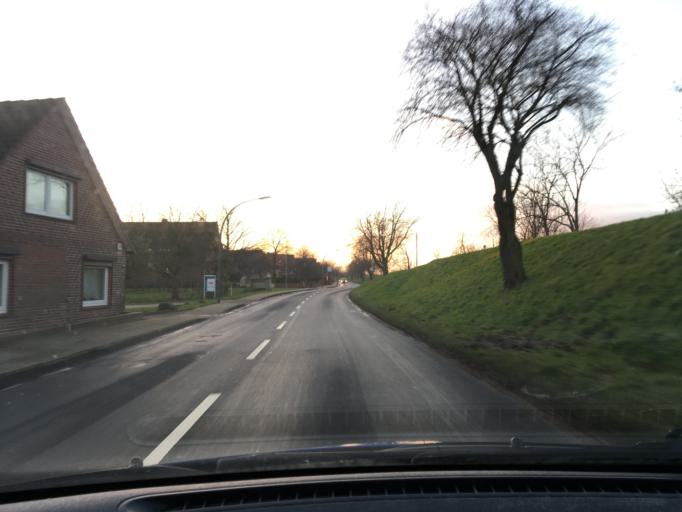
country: DE
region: Hamburg
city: Altona
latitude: 53.5092
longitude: 9.8720
